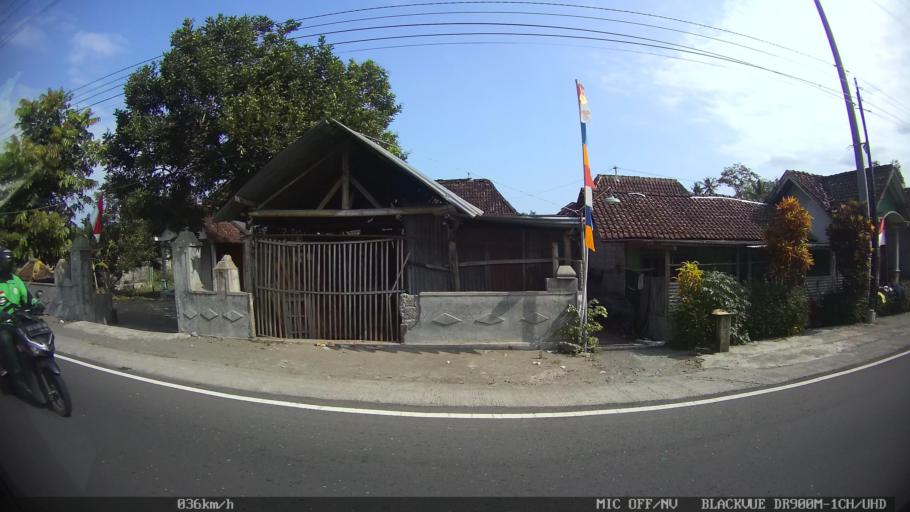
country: ID
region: Daerah Istimewa Yogyakarta
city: Depok
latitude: -7.7268
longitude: 110.4329
